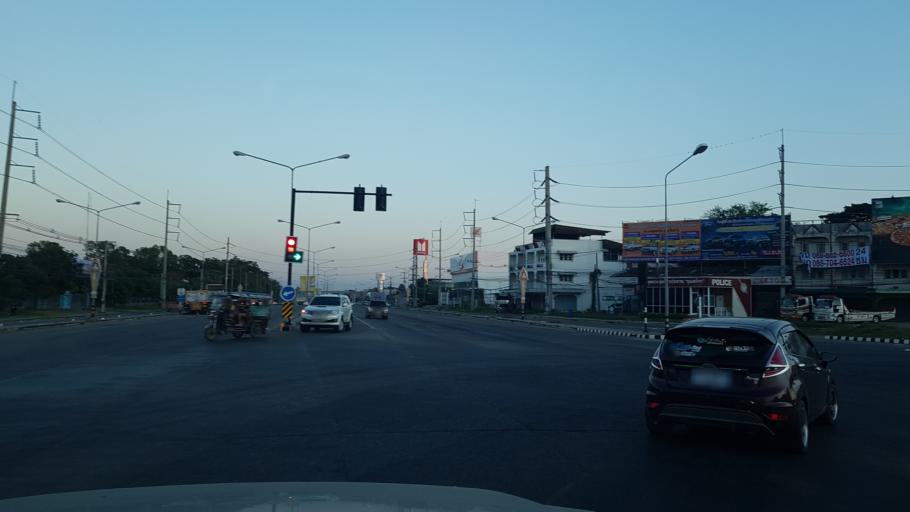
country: TH
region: Khon Kaen
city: Chum Phae
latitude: 16.5412
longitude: 102.1083
